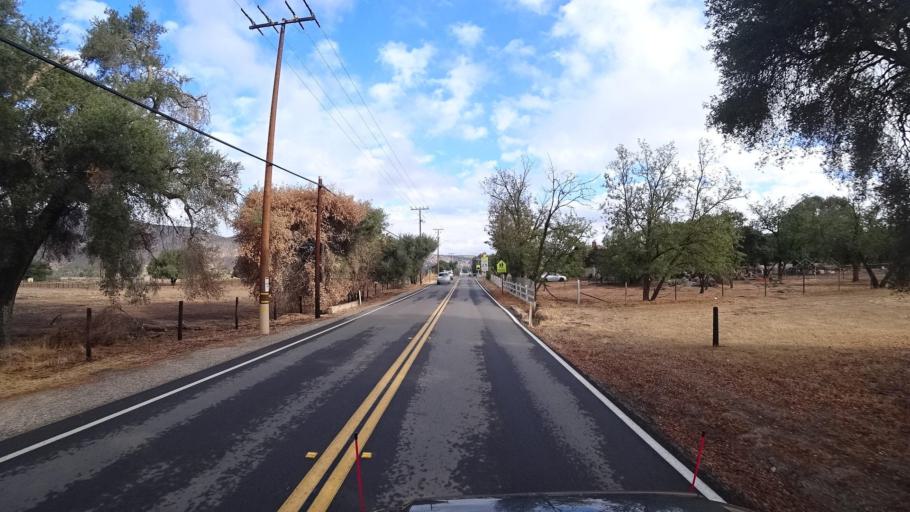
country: MX
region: Baja California
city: Tecate
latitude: 32.6076
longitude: -116.6132
